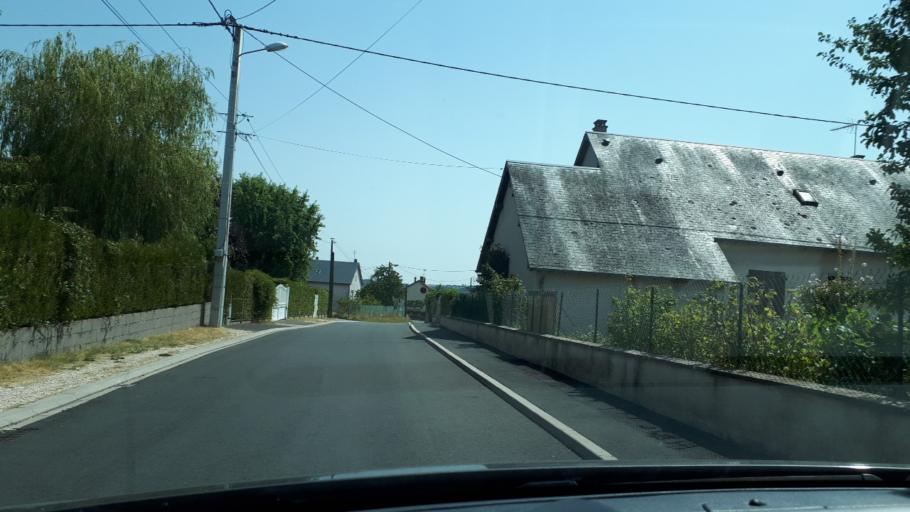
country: FR
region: Centre
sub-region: Departement du Loir-et-Cher
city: Vendome
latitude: 47.8140
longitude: 1.0632
